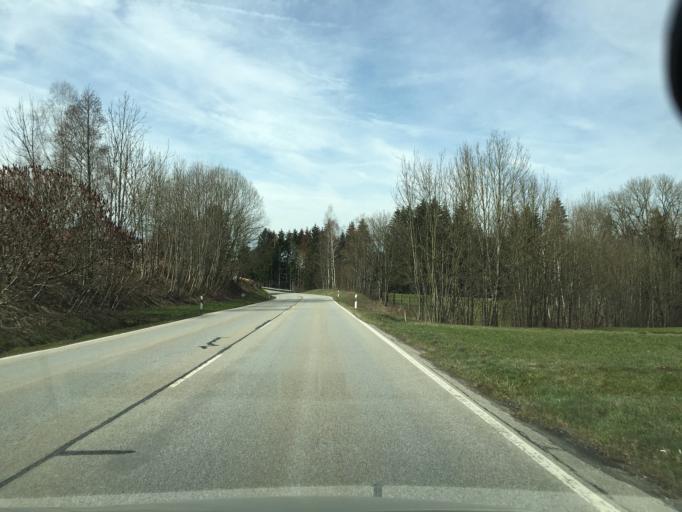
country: DE
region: Bavaria
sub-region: Upper Bavaria
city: Siegsdorf
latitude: 47.8183
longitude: 12.6732
